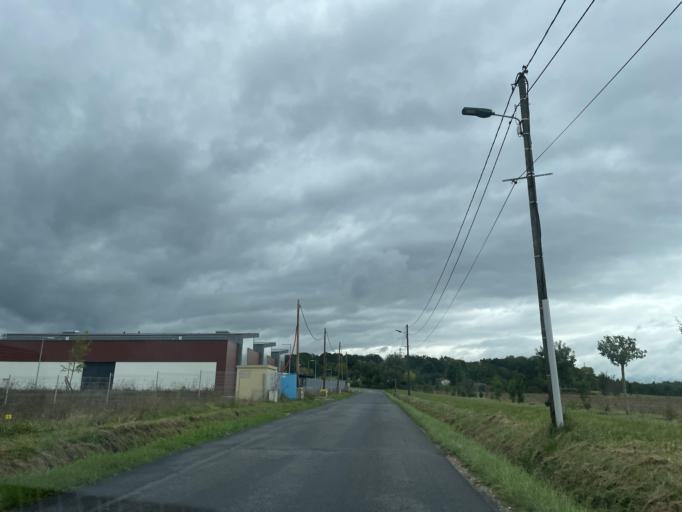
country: FR
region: Ile-de-France
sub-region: Departement de Seine-et-Marne
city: Coulommiers
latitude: 48.8138
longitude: 3.1096
